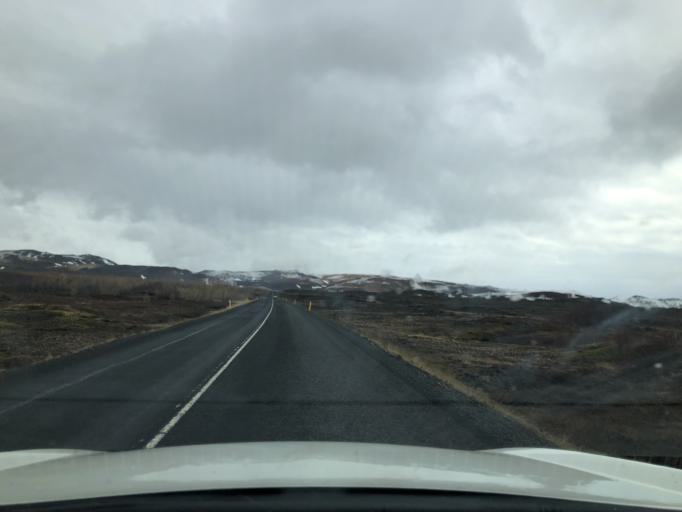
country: IS
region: Northeast
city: Laugar
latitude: 65.6388
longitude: -16.8885
